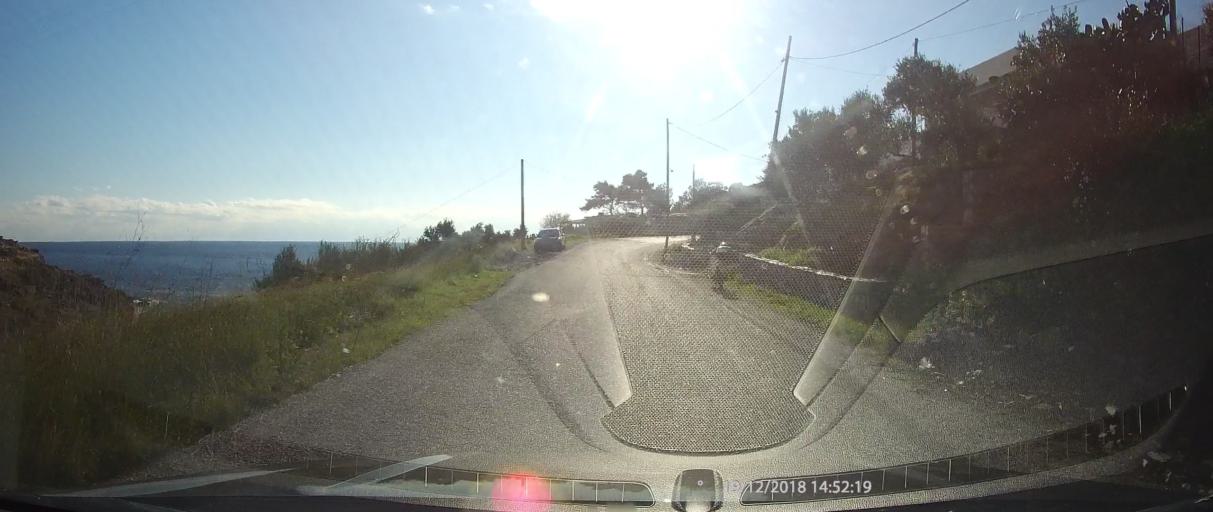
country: GR
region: Peloponnese
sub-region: Nomos Lakonias
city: Gytheio
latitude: 36.4608
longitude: 22.4435
